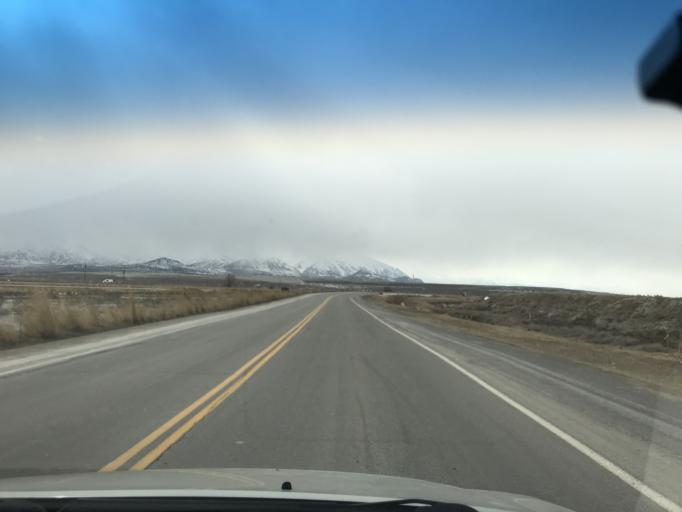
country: US
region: Utah
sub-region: Salt Lake County
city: Magna
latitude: 40.7728
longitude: -112.0653
